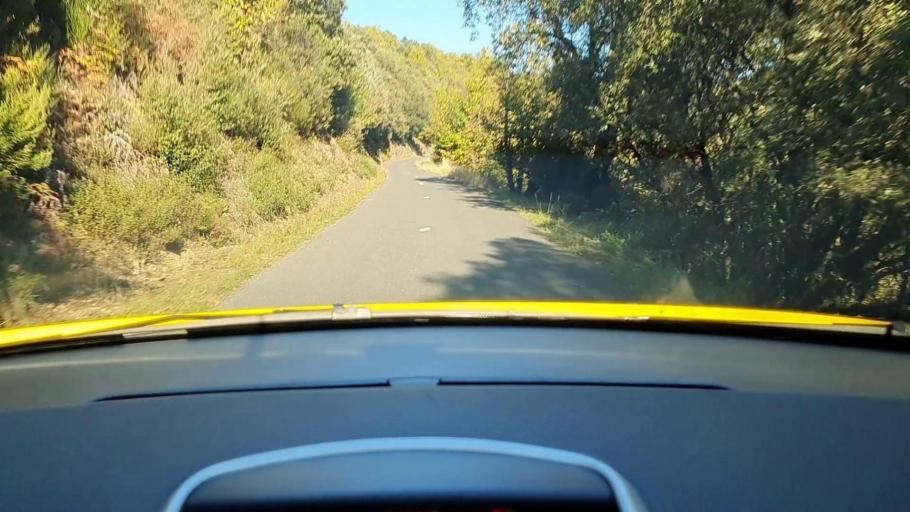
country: FR
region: Languedoc-Roussillon
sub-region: Departement du Gard
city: Sumene
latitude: 44.0221
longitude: 3.7514
